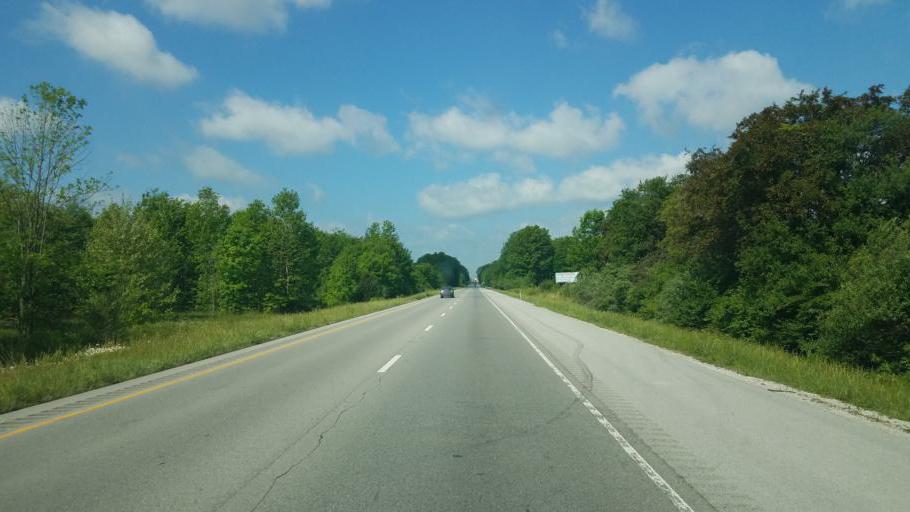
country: US
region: Indiana
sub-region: Putnam County
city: Cloverdale
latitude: 39.5423
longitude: -86.7455
